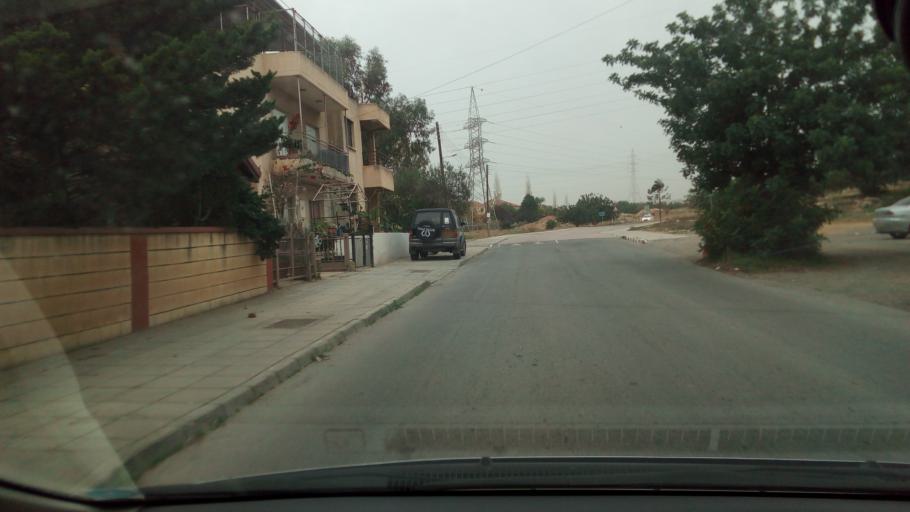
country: CY
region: Limassol
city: Pano Polemidia
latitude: 34.6959
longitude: 32.9855
